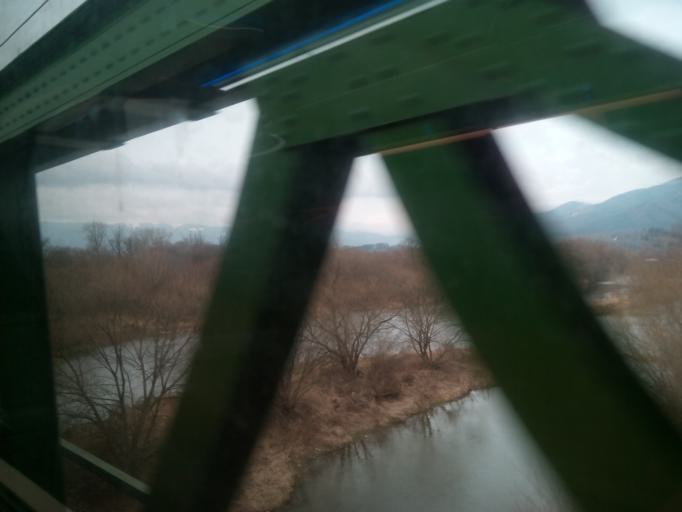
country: SK
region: Zilinsky
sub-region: Okres Martin
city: Martin
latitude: 49.1046
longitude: 19.0232
